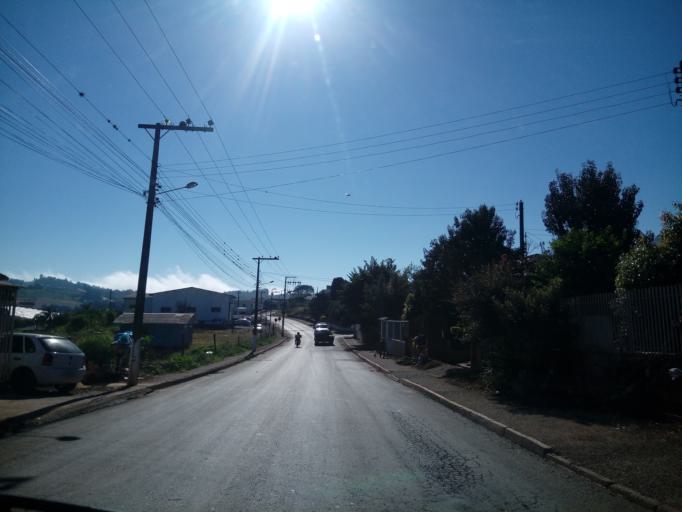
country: BR
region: Santa Catarina
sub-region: Chapeco
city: Chapeco
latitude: -27.0687
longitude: -52.6074
